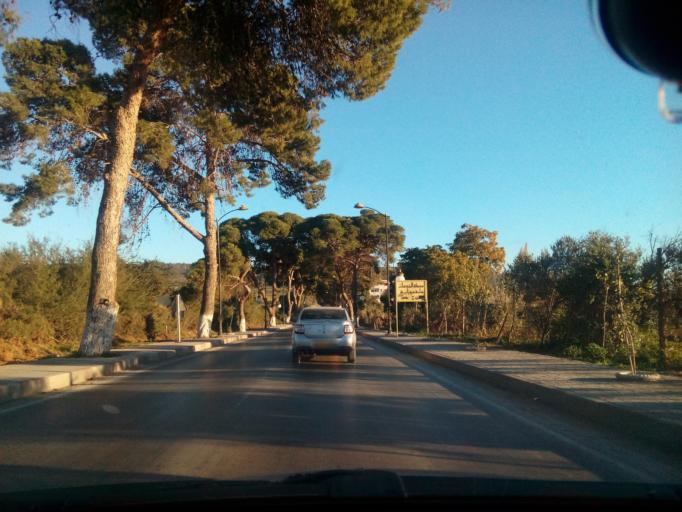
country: DZ
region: Mostaganem
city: Mostaganem
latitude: 35.7766
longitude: 0.1952
